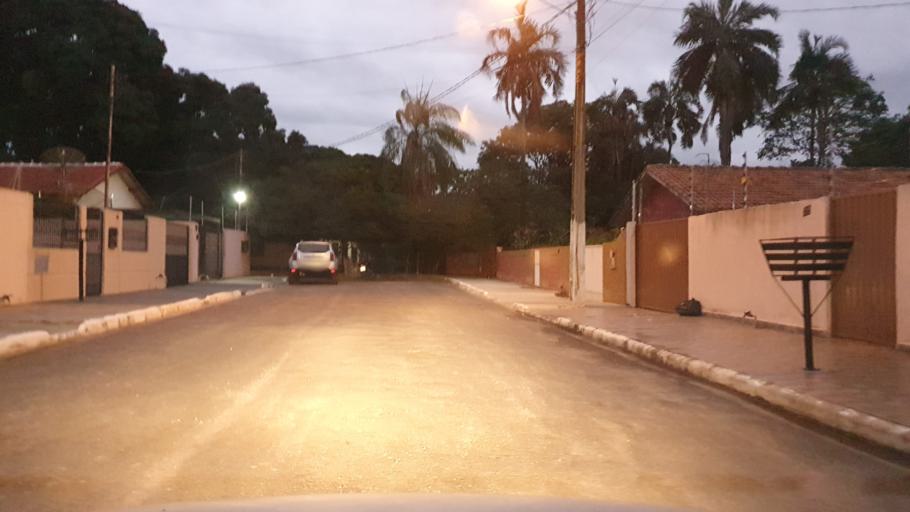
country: BR
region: Mato Grosso
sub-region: Pontes E Lacerda
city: Pontes e Lacerda
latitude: -15.2326
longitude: -59.3155
